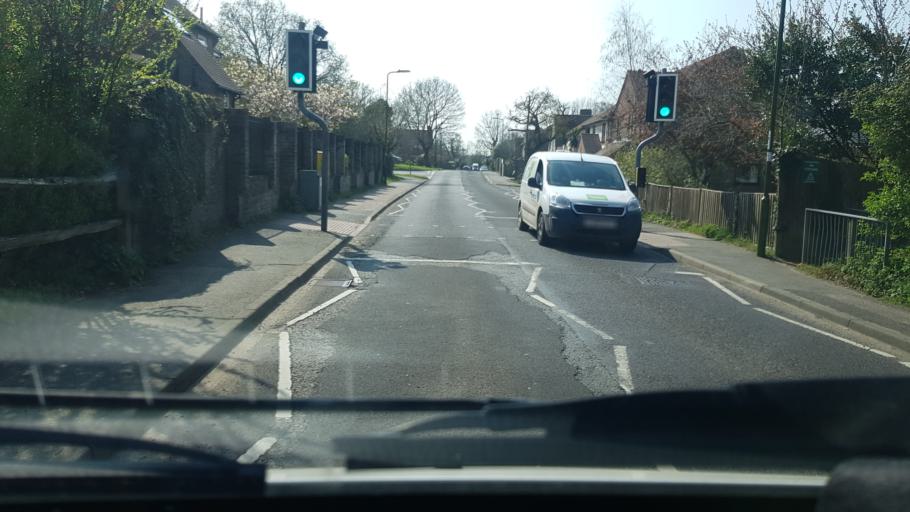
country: GB
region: England
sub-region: West Sussex
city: Chichester
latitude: 50.8383
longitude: -0.8145
